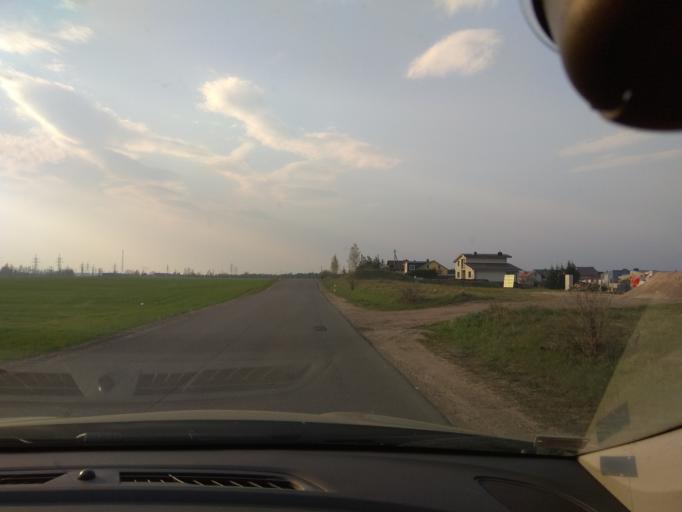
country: LT
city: Baltoji Voke
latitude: 54.6055
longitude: 25.1324
